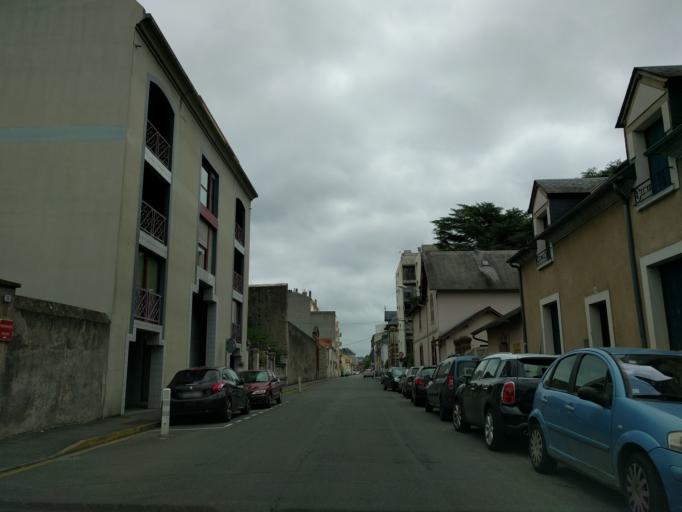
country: FR
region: Midi-Pyrenees
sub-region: Departement des Hautes-Pyrenees
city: Tarbes
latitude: 43.2348
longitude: 0.0784
